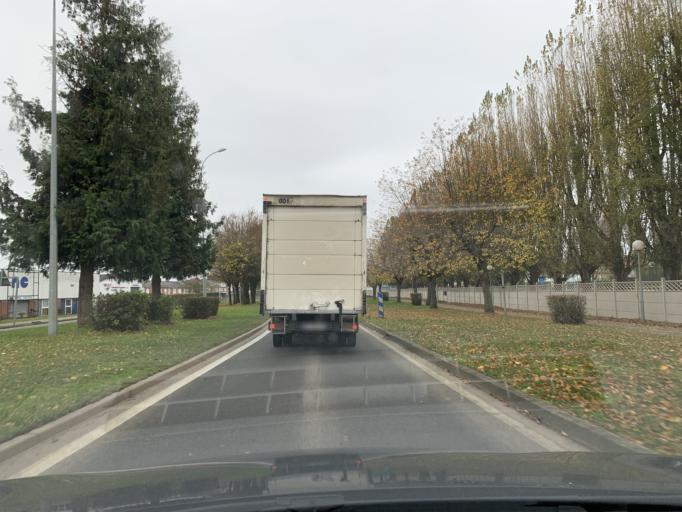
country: FR
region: Nord-Pas-de-Calais
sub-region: Departement du Nord
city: Neuville-Saint-Remy
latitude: 50.1919
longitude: 3.2136
